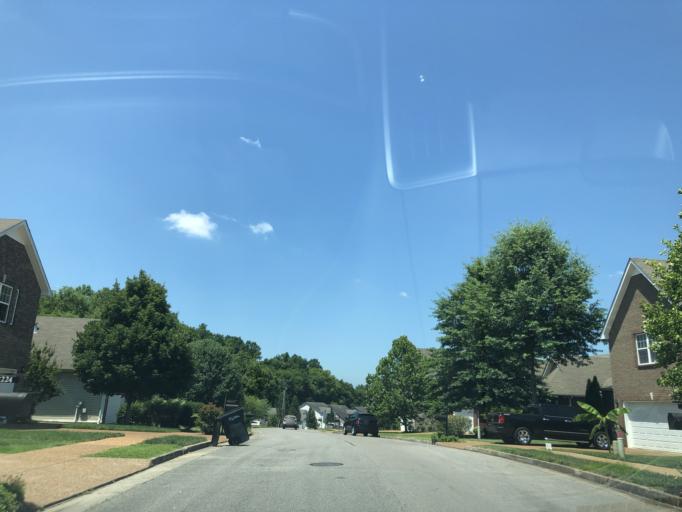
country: US
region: Tennessee
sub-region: Williamson County
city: Nolensville
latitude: 36.0191
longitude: -86.6701
